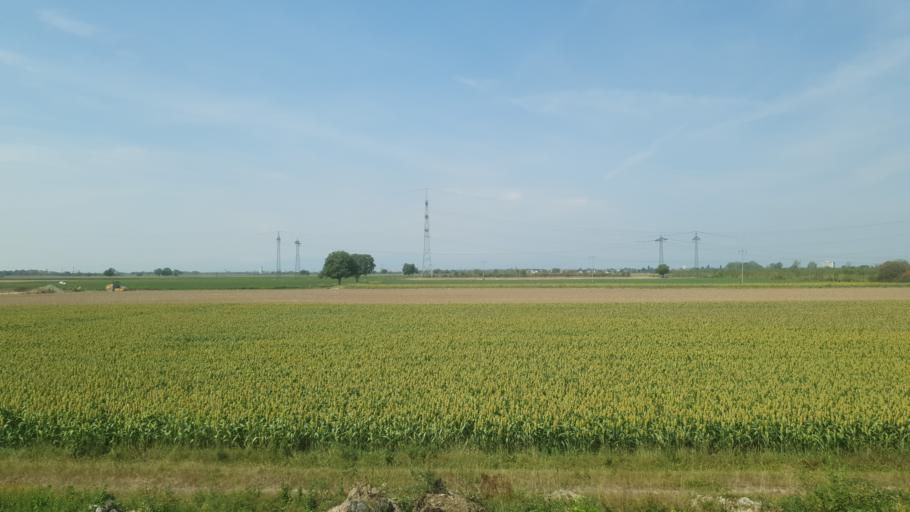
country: DE
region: Baden-Wuerttemberg
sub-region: Freiburg Region
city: Auggen
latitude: 47.7979
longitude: 7.5919
